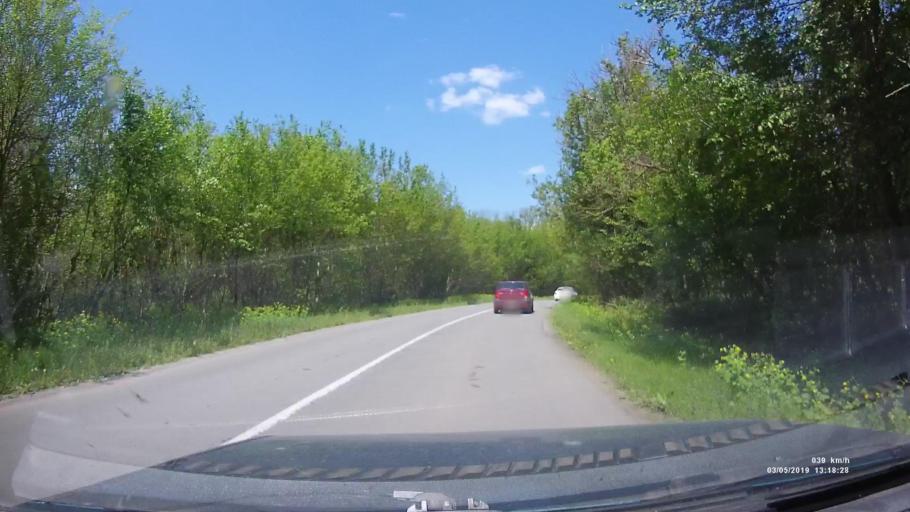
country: RU
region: Rostov
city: Semikarakorsk
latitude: 47.5328
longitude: 40.7484
